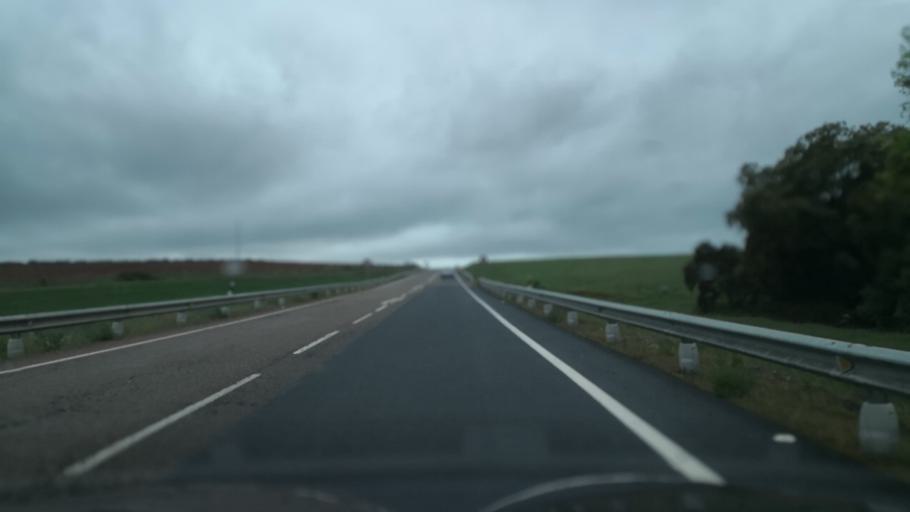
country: ES
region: Extremadura
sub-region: Provincia de Badajoz
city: La Roca de la Sierra
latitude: 39.0573
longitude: -6.7753
